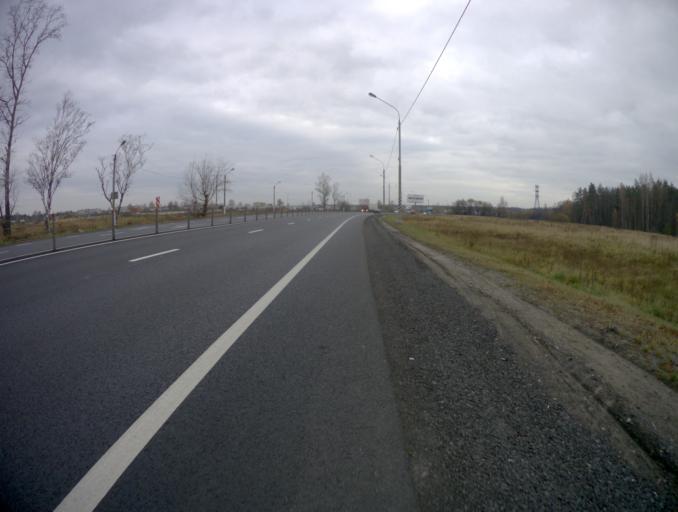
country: RU
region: Moskovskaya
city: Malaya Dubna
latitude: 55.8714
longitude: 38.9633
